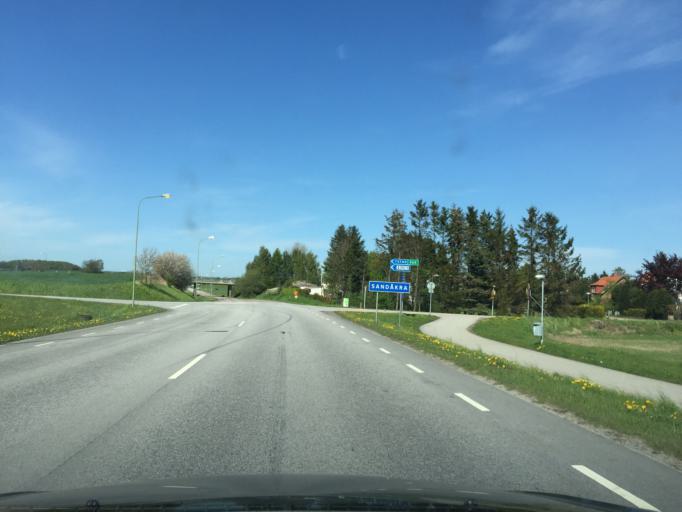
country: SE
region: Skane
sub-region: Skurups Kommun
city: Skurup
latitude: 55.4921
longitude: 13.5081
